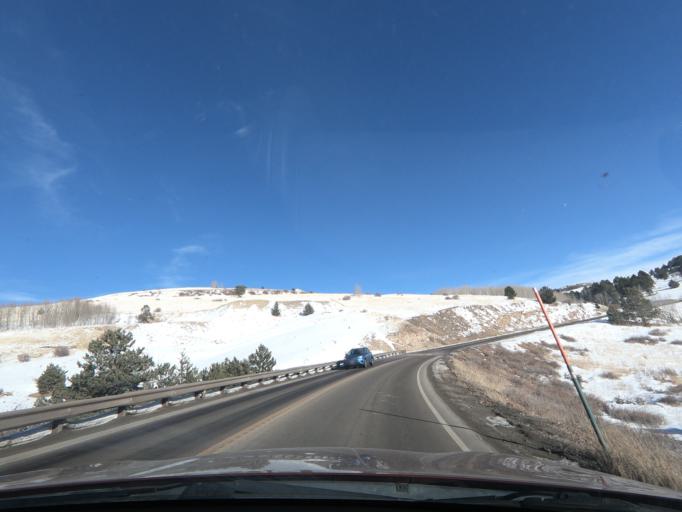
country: US
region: Colorado
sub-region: Teller County
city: Cripple Creek
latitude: 38.7551
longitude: -105.1659
